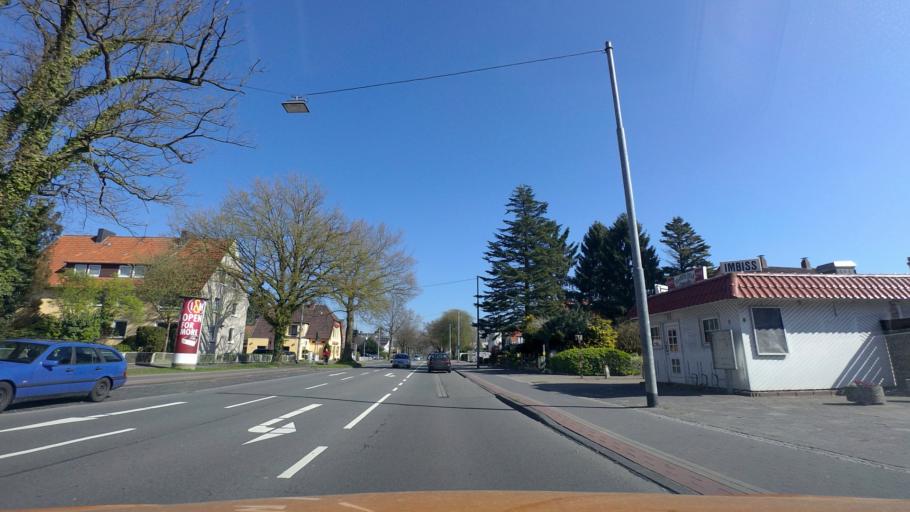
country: DE
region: Lower Saxony
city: Oldenburg
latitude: 53.1050
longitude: 8.2061
